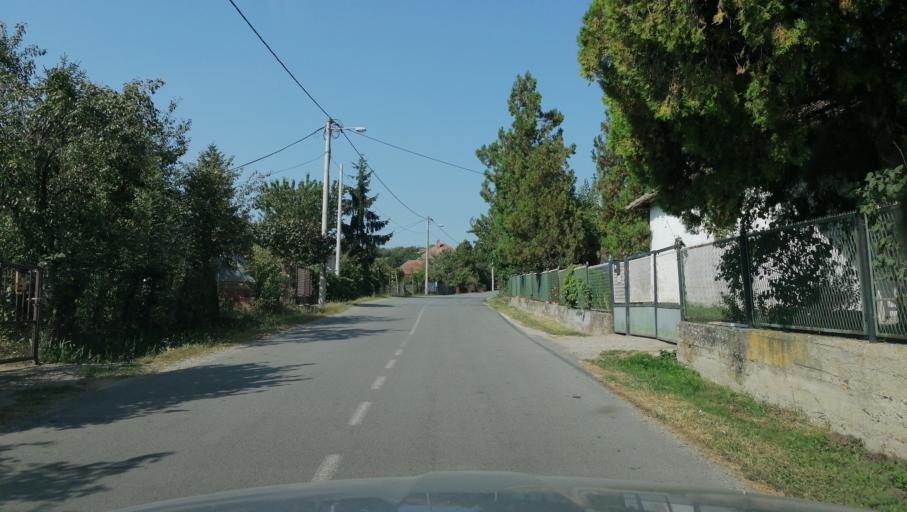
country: RS
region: Central Serbia
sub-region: Belgrade
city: Sopot
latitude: 44.5891
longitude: 20.6101
